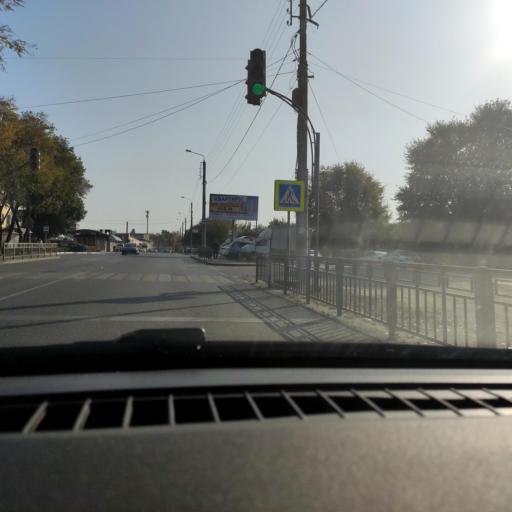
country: RU
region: Voronezj
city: Voronezh
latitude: 51.6286
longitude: 39.1757
